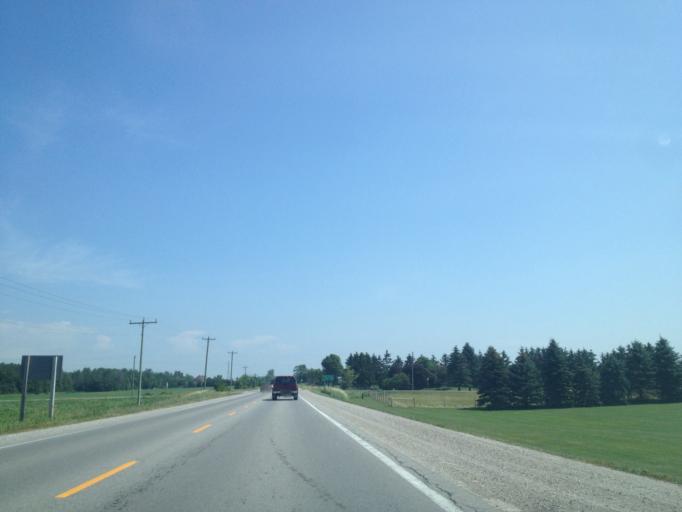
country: CA
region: Ontario
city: Huron East
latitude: 43.4354
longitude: -81.2257
